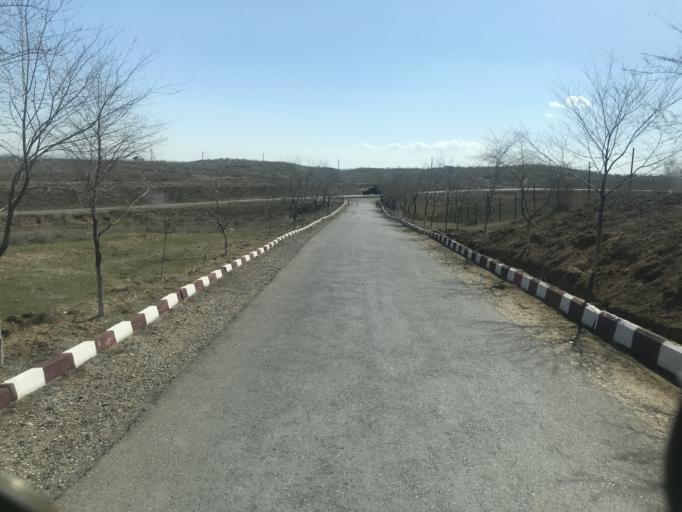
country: KZ
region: Ongtustik Qazaqstan
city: Shardara
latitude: 41.2479
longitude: 67.9023
